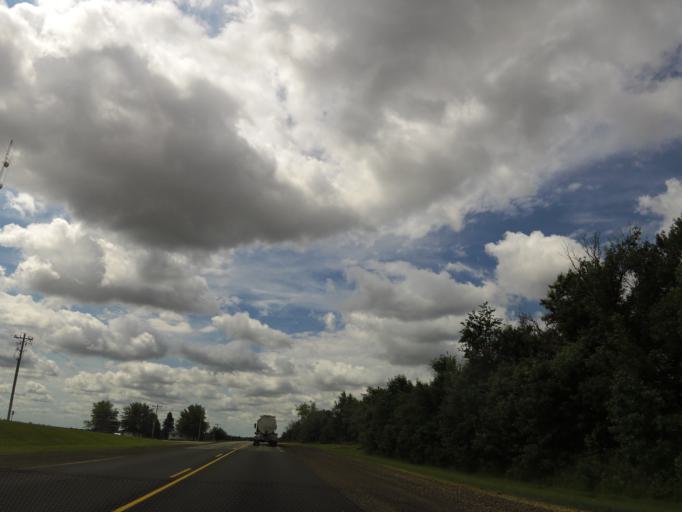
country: US
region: Iowa
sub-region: Howard County
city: Cresco
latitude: 43.2862
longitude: -92.2989
